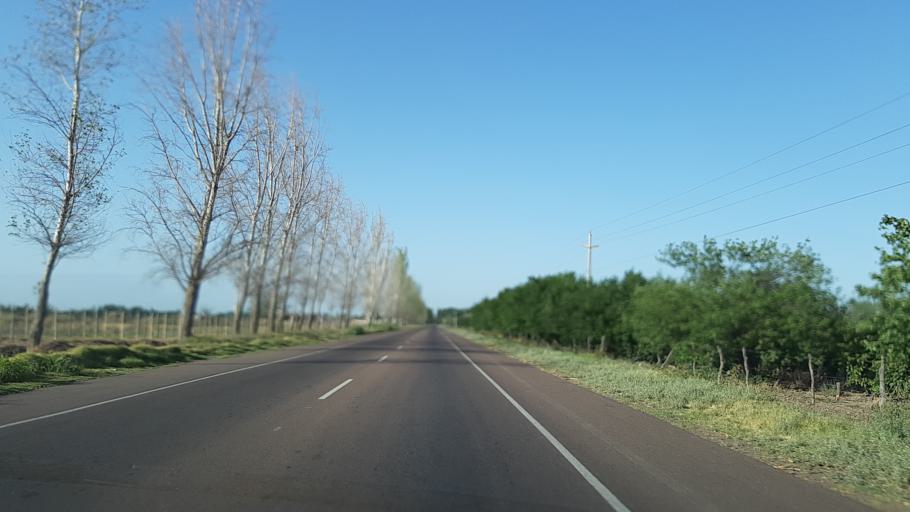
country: AR
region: Mendoza
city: San Martin
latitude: -32.9505
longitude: -68.4288
